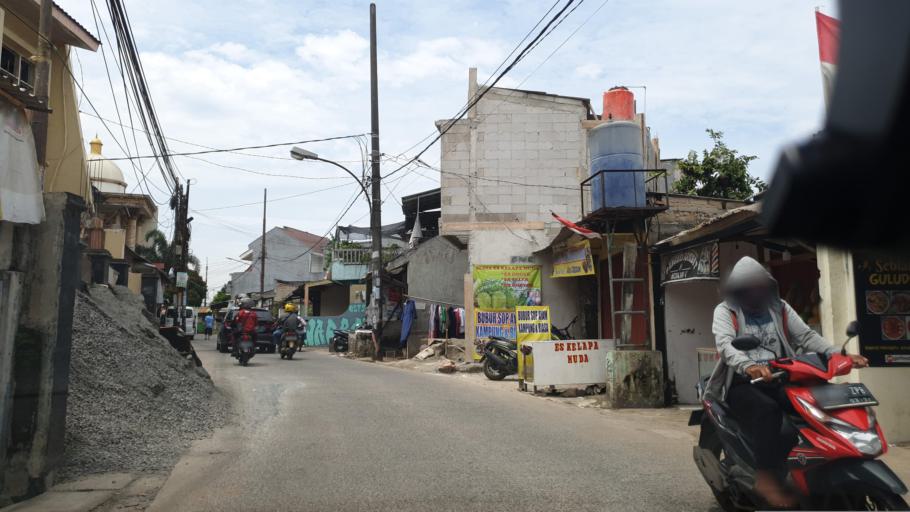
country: ID
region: West Java
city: Pamulang
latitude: -6.3660
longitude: 106.7505
